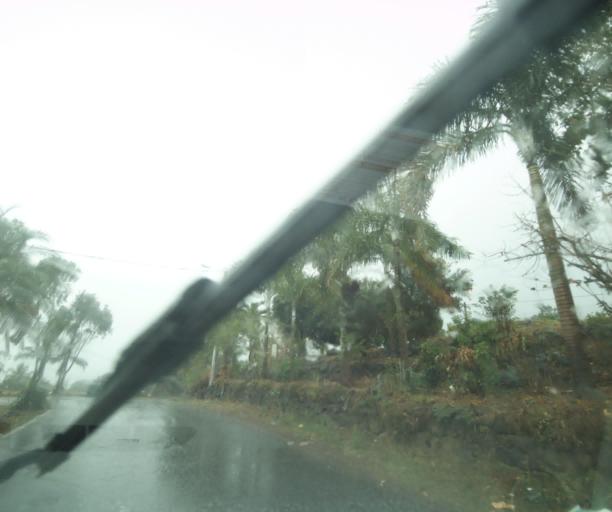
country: RE
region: Reunion
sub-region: Reunion
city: La Possession
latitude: -20.9848
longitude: 55.3261
